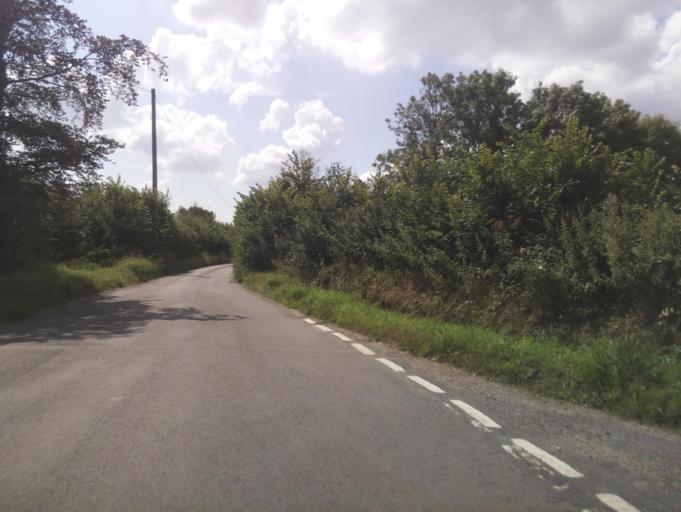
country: GB
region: England
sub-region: Wiltshire
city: Hankerton
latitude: 51.6142
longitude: -2.0461
